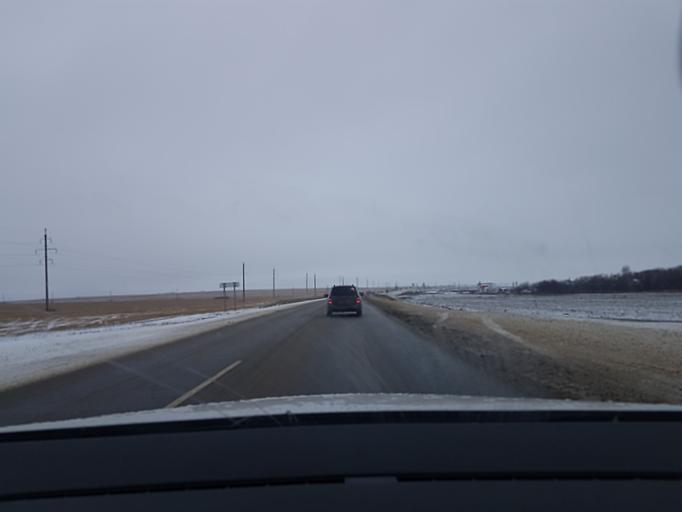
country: RU
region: Rjazan
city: Vilenka
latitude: 54.3327
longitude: 38.8025
